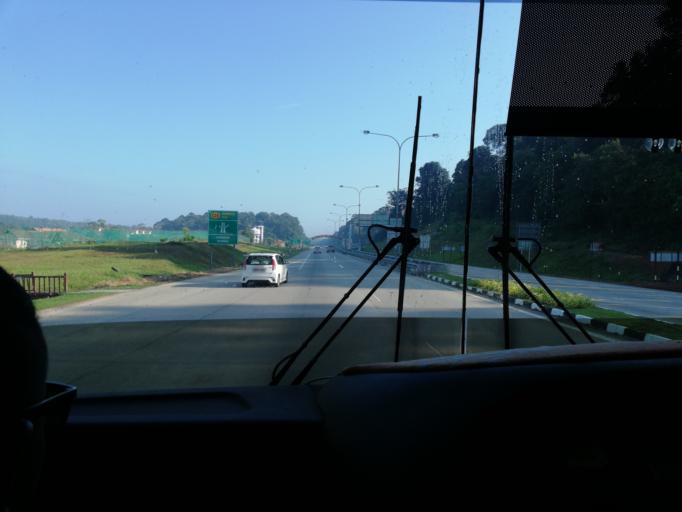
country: MY
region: Negeri Sembilan
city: Port Dickson
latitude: 2.5011
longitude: 101.8655
